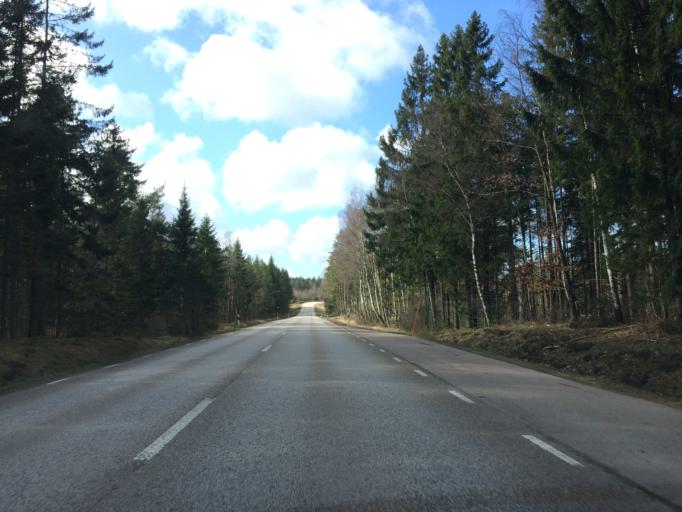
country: SE
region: Kronoberg
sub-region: Markaryds Kommun
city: Markaryd
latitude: 56.4763
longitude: 13.5025
